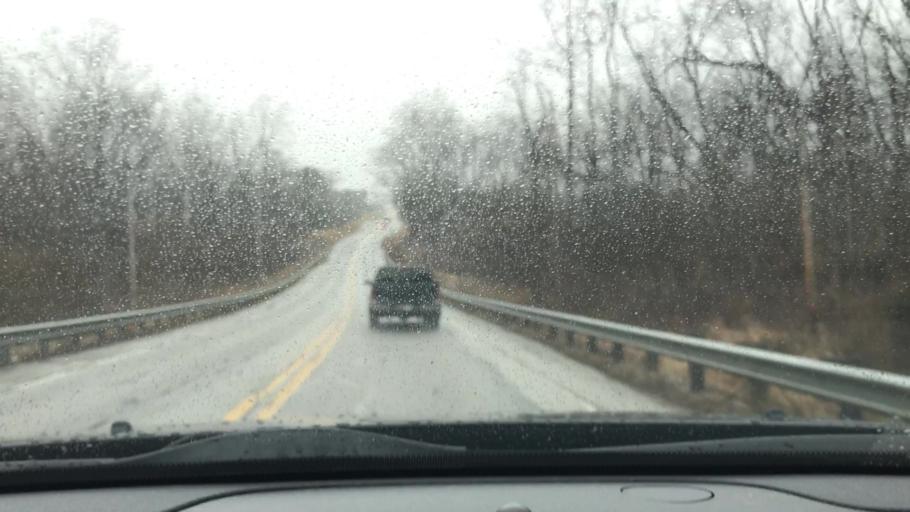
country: US
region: Indiana
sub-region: Morgan County
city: Mooresville
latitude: 39.5964
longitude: -86.3449
